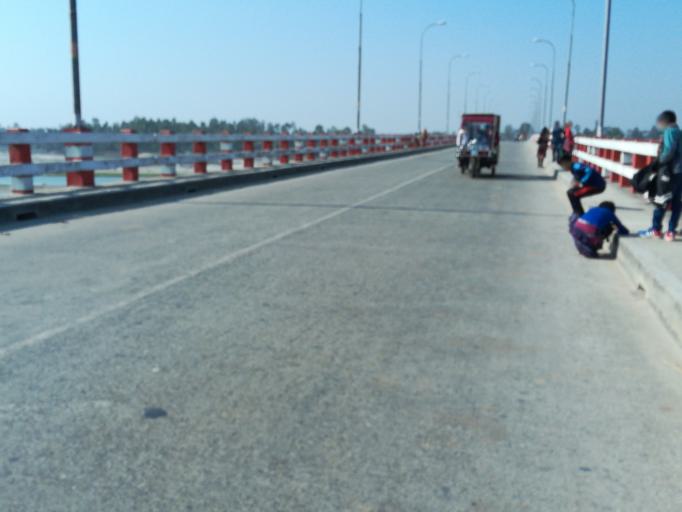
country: BD
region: Rangpur Division
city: Nageswari
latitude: 25.8200
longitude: 89.6703
